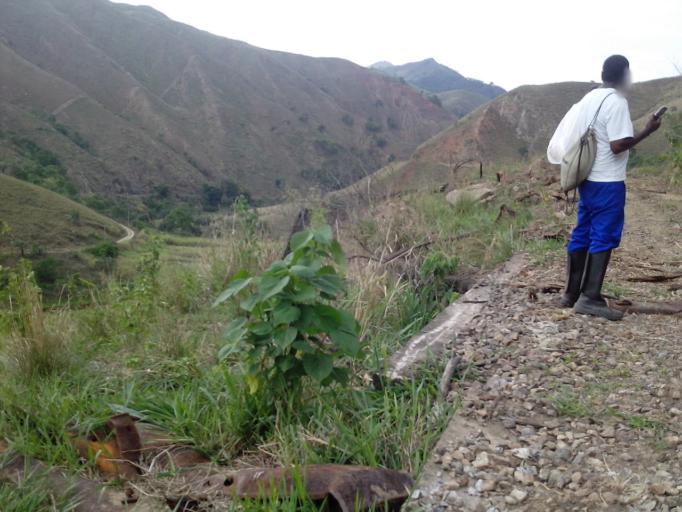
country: BR
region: Rio de Janeiro
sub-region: Miguel Pereira
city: Miguel Pereira
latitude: -22.4992
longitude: -43.4980
